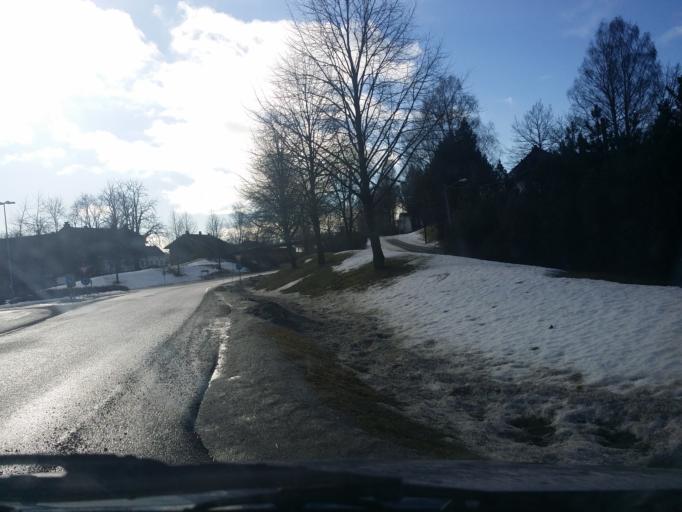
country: NO
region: Buskerud
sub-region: Lier
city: Lierbyen
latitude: 59.7884
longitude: 10.2410
